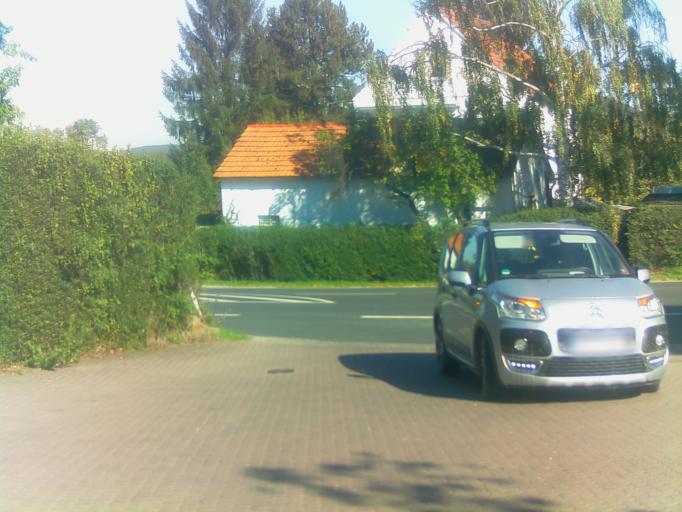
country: DE
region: Thuringia
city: Kahla
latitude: 50.8095
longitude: 11.5777
